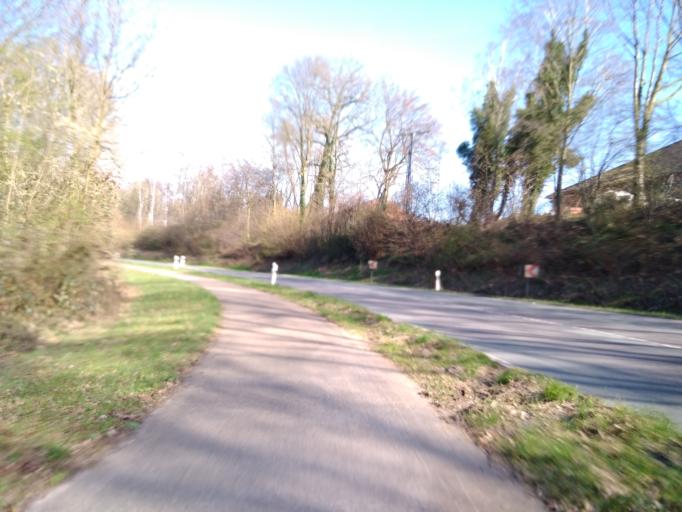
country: DE
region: North Rhine-Westphalia
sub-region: Regierungsbezirk Dusseldorf
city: Schermbeck
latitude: 51.6696
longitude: 6.8383
